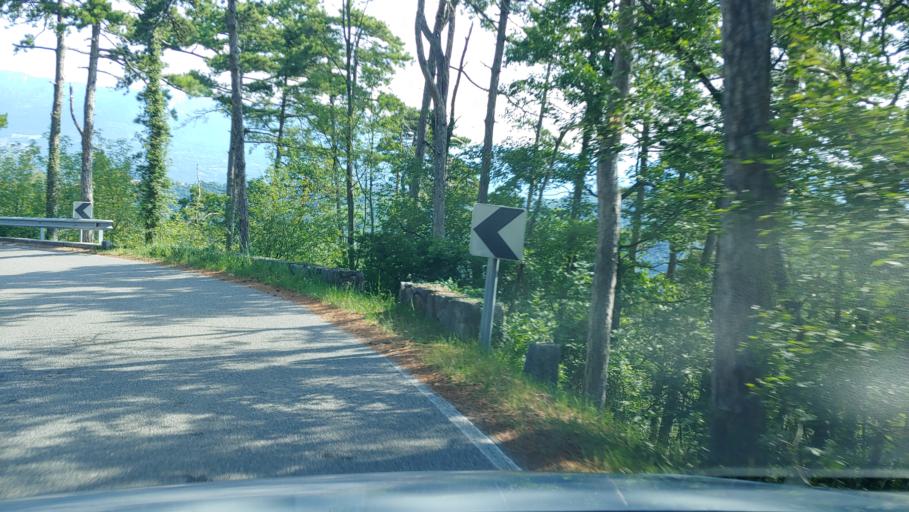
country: SI
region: Komen
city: Komen
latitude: 45.8483
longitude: 13.7881
